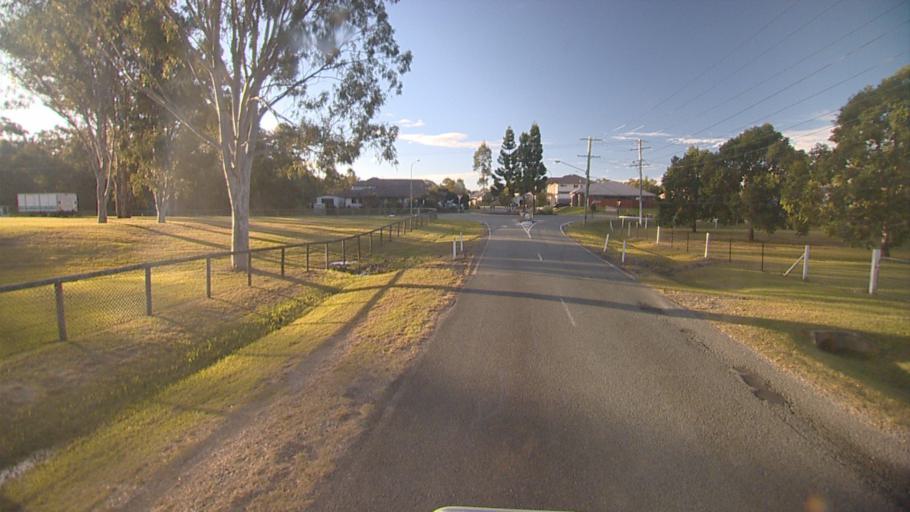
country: AU
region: Queensland
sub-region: Logan
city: Waterford West
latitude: -27.7189
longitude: 153.1426
